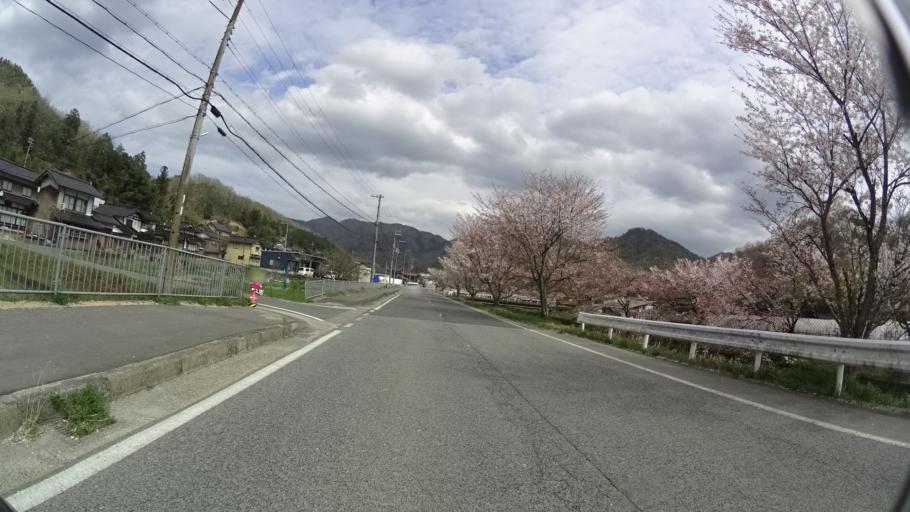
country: JP
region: Hyogo
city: Toyooka
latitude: 35.5021
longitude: 134.8770
